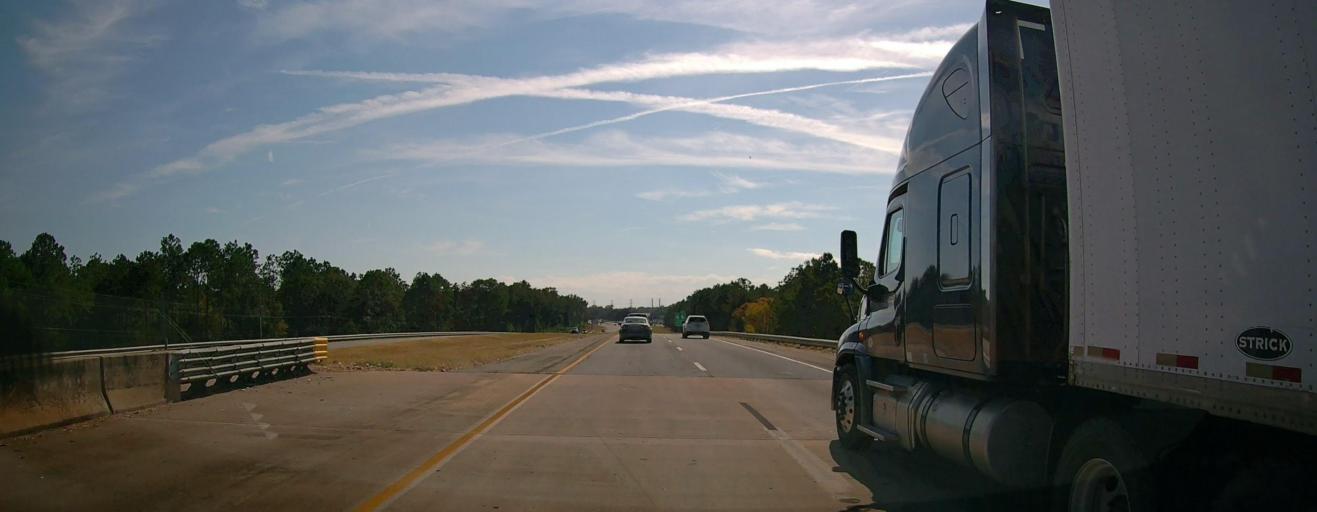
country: US
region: Georgia
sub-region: Dougherty County
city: Albany
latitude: 31.5634
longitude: -84.1135
